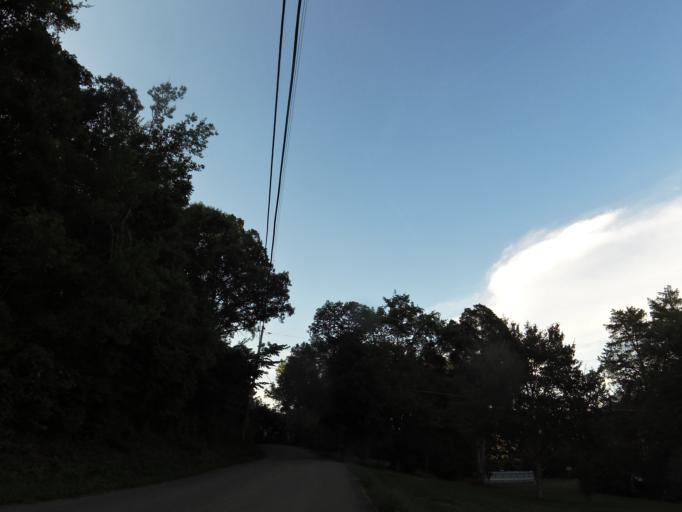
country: US
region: Tennessee
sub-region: Knox County
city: Knoxville
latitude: 35.9091
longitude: -83.9101
